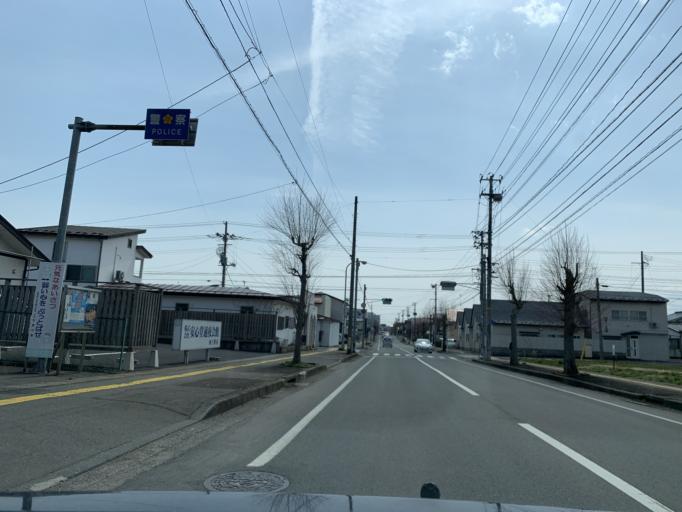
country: JP
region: Iwate
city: Mizusawa
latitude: 39.1327
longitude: 141.1366
